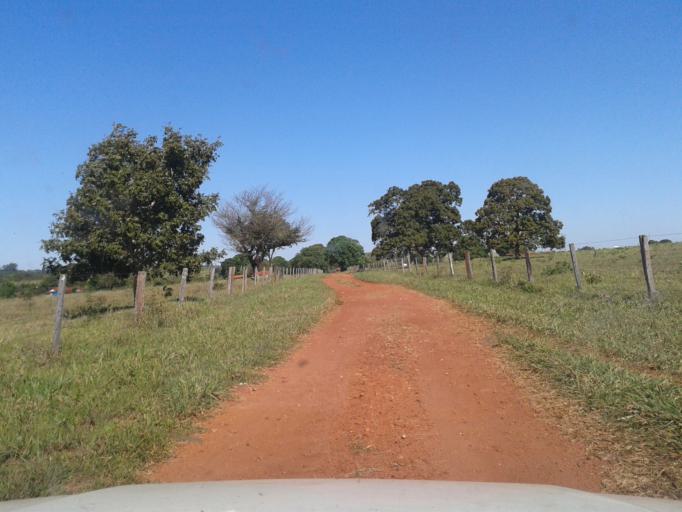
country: BR
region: Minas Gerais
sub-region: Santa Vitoria
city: Santa Vitoria
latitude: -19.0324
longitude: -50.3772
